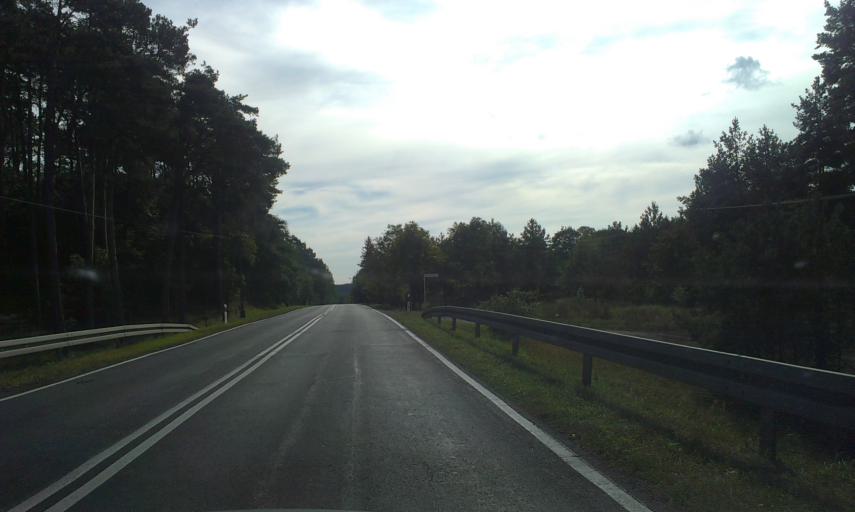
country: PL
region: Greater Poland Voivodeship
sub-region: Powiat zlotowski
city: Okonek
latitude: 53.5441
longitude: 16.8439
